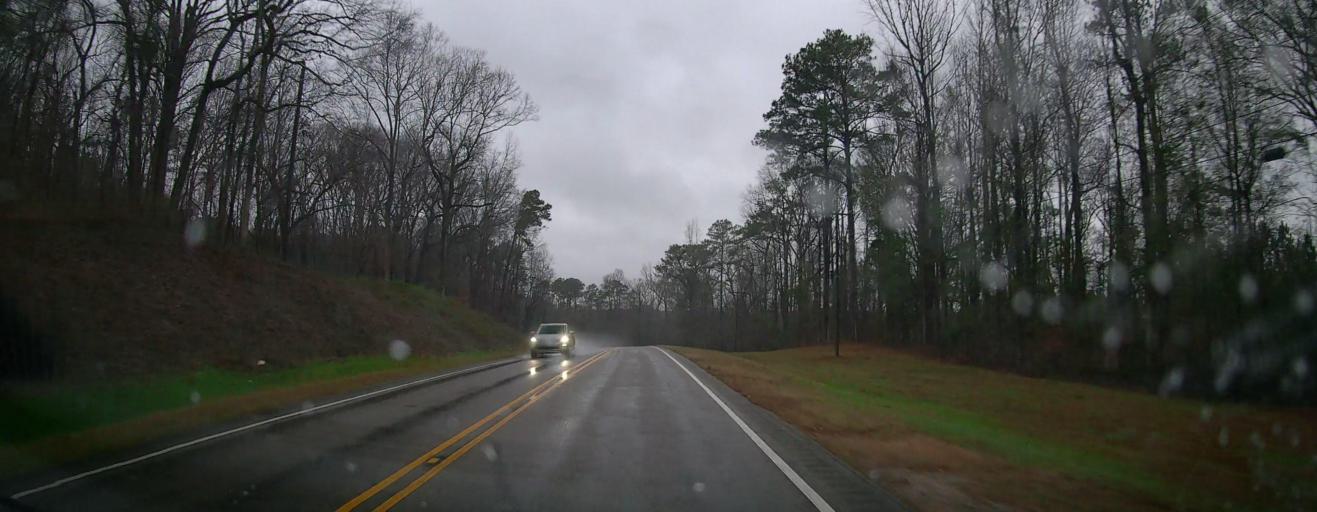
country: US
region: Alabama
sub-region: Autauga County
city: Prattville
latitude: 32.4886
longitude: -86.5422
